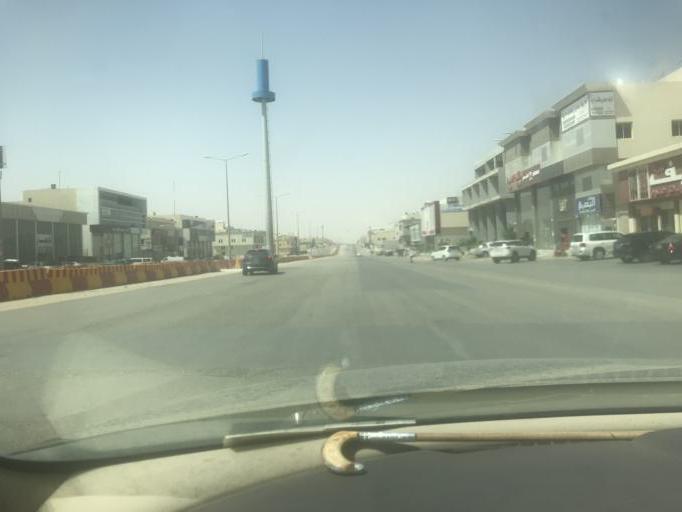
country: SA
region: Ar Riyad
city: Riyadh
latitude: 24.8122
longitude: 46.5998
